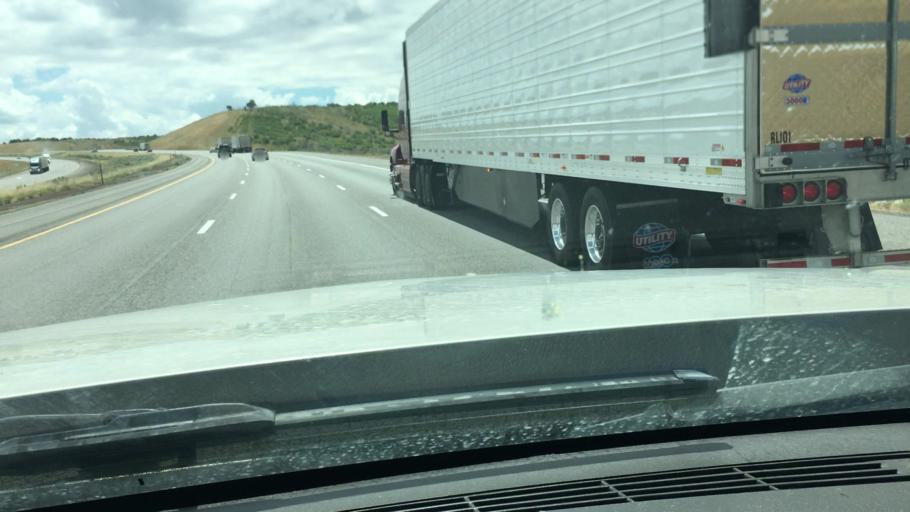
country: US
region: Utah
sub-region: Beaver County
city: Beaver
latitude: 38.4874
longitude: -112.6183
